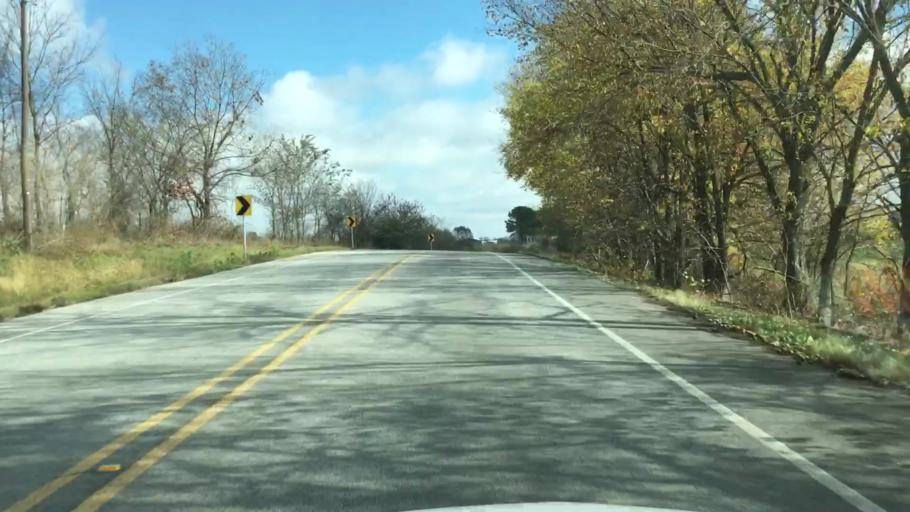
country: US
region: Arkansas
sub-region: Benton County
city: Centerton
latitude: 36.3024
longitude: -94.3178
